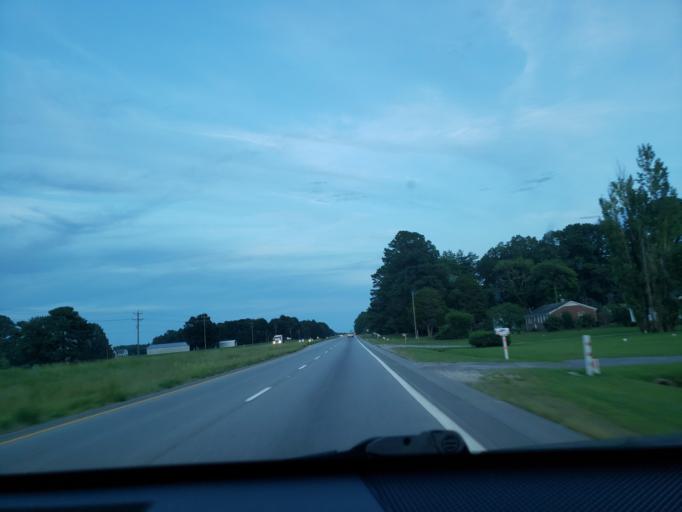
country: US
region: Virginia
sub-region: Southampton County
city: Courtland
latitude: 36.7045
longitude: -77.1196
